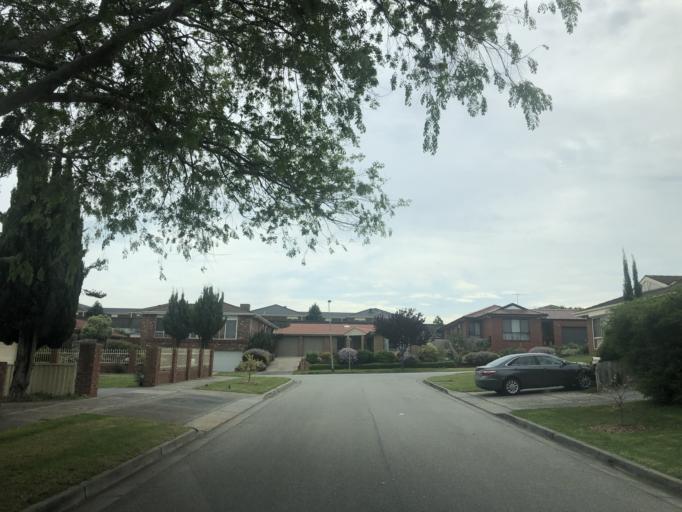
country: AU
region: Victoria
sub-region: Casey
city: Hallam
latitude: -38.0050
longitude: 145.2777
